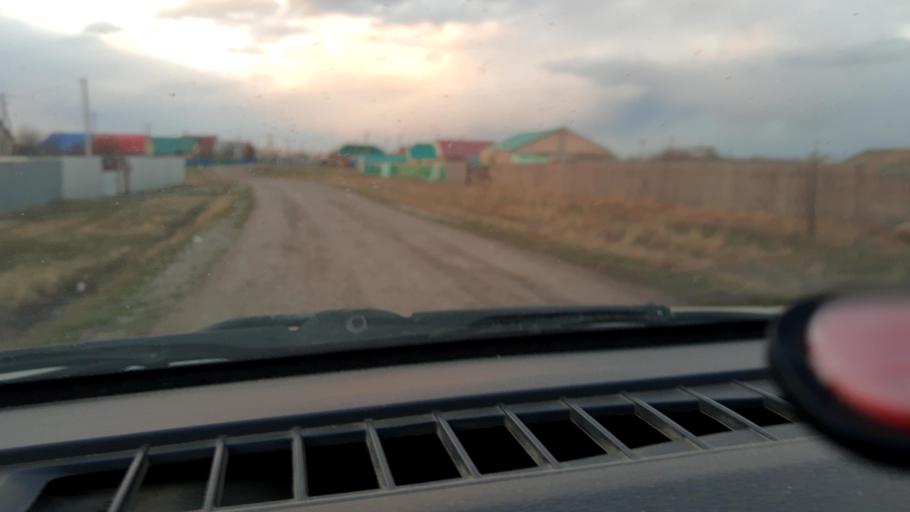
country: RU
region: Bashkortostan
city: Asanovo
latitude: 54.9037
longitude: 55.4847
